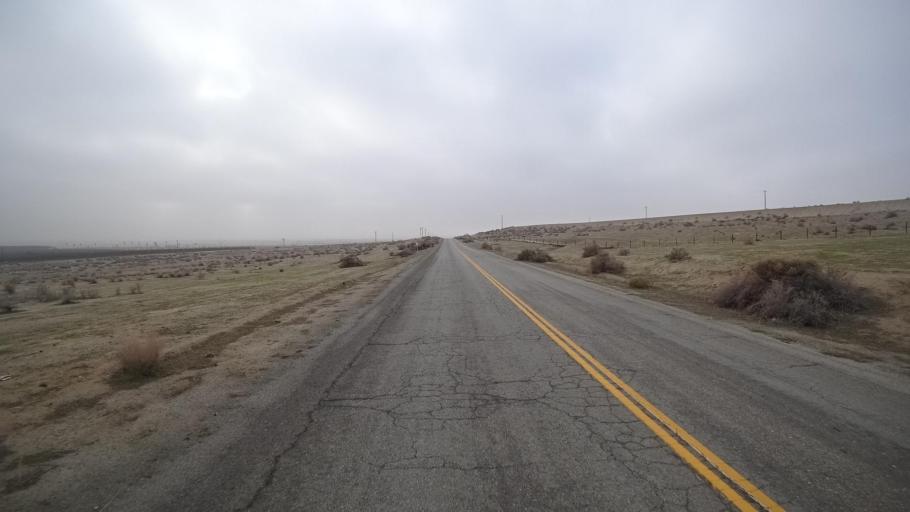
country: US
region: California
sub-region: Kern County
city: Maricopa
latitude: 35.1331
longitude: -119.3559
